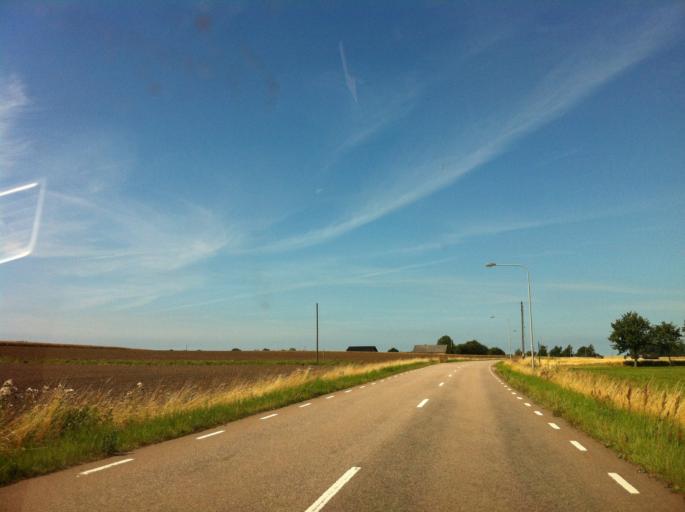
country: SE
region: Skane
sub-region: Helsingborg
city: Glumslov
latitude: 55.9363
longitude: 12.8605
